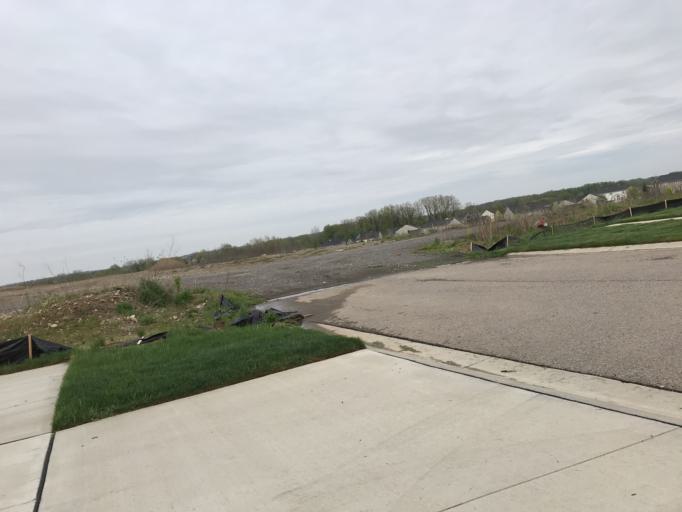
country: US
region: Michigan
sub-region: Oakland County
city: South Lyon
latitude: 42.4782
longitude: -83.6296
